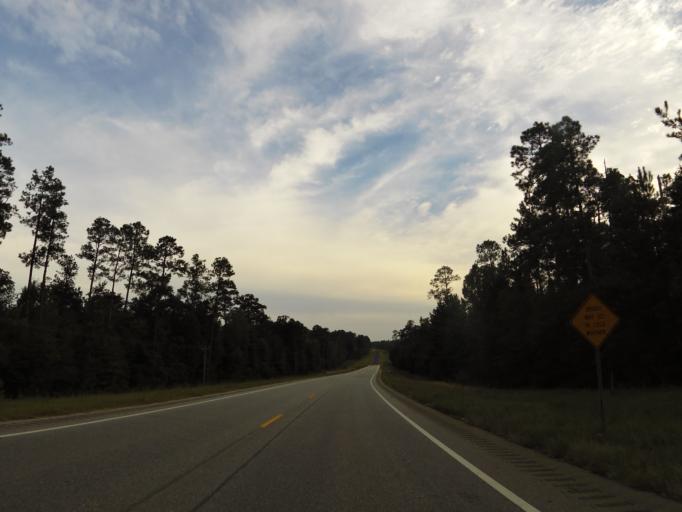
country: US
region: Alabama
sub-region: Monroe County
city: Frisco City
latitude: 31.2580
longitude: -87.4931
